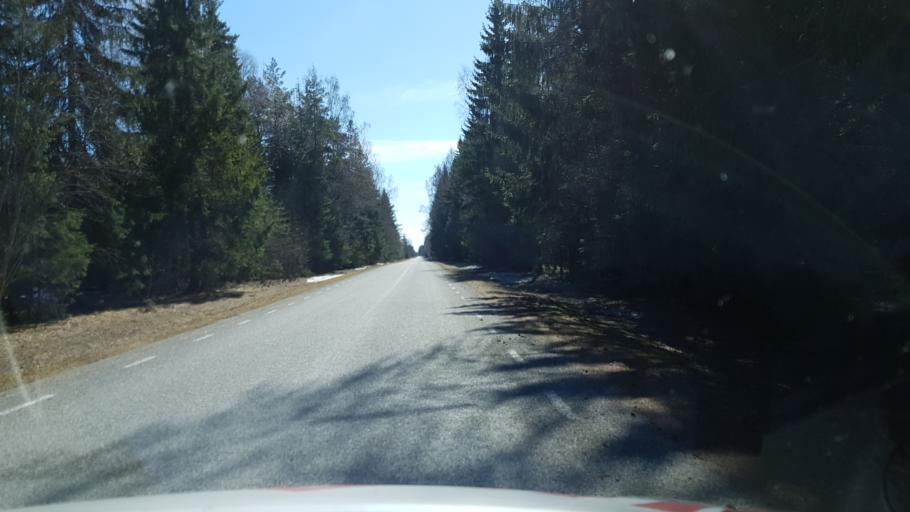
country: EE
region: Laeaene-Virumaa
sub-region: Vinni vald
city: Vinni
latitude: 59.1706
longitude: 26.5074
